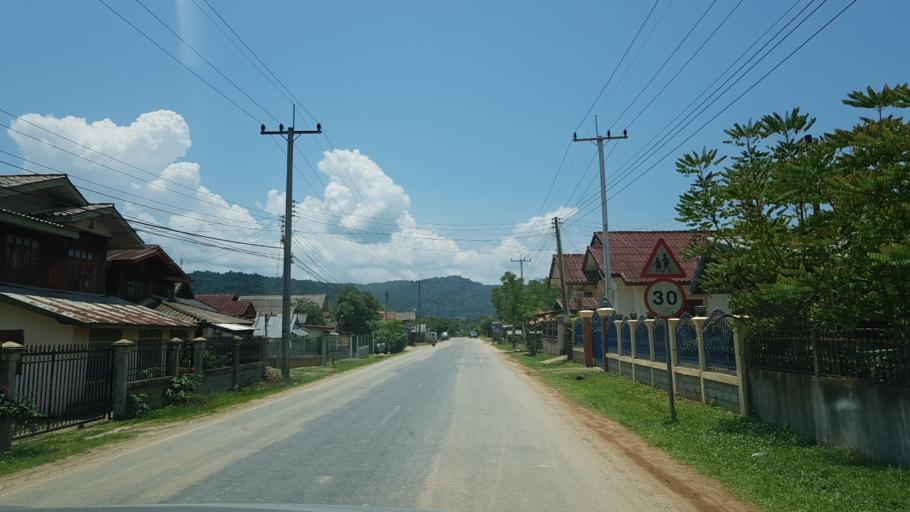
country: LA
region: Vientiane
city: Muang Kasi
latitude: 19.2451
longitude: 102.2490
